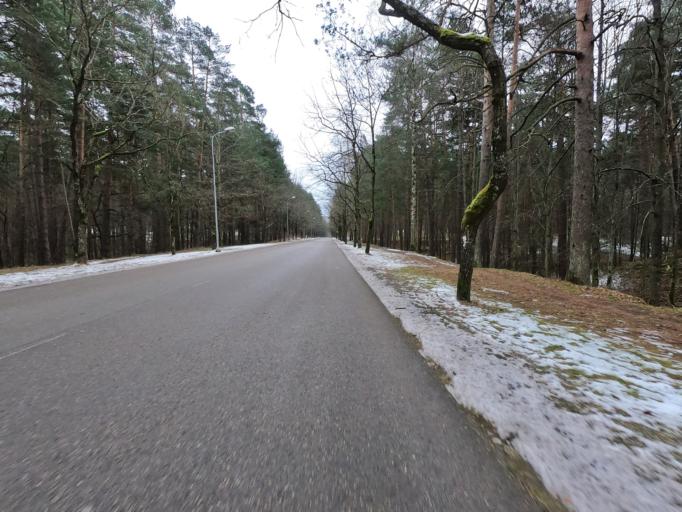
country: LV
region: Riga
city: Jaunciems
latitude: 57.0169
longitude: 24.1438
